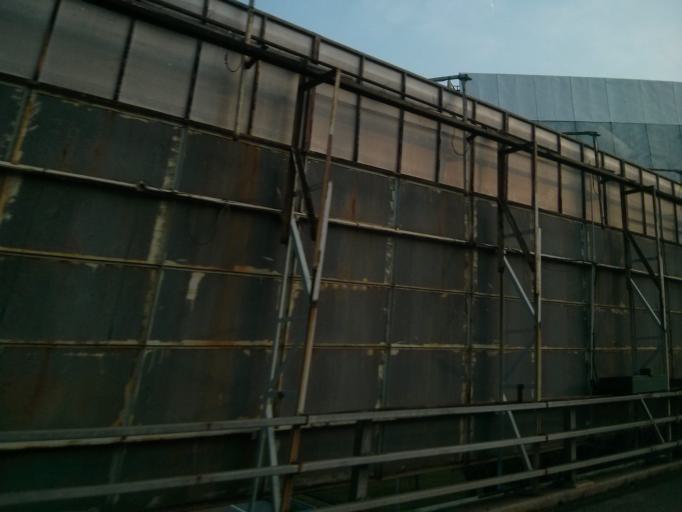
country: MY
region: Negeri Sembilan
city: Kampung Baharu Nilai
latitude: 2.7831
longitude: 101.6739
